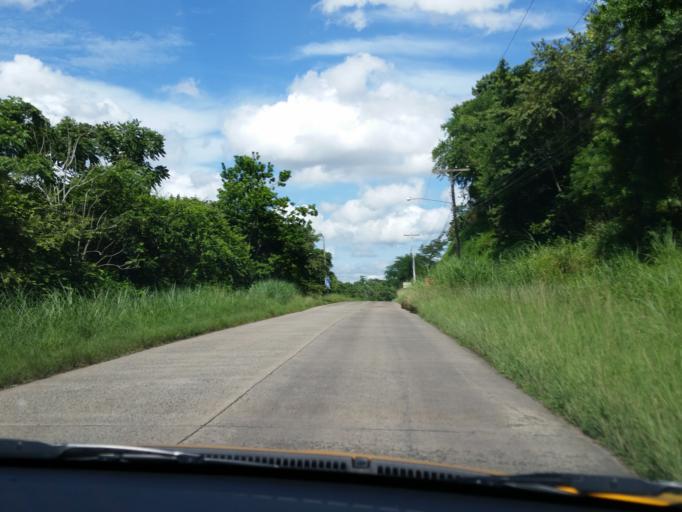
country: PA
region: Panama
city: San Miguelito
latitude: 9.0723
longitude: -79.4686
